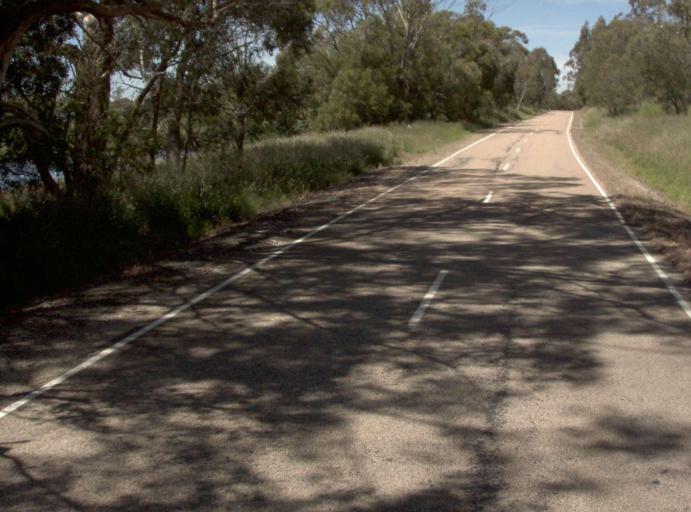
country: AU
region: Victoria
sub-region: East Gippsland
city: Lakes Entrance
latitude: -37.1813
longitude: 148.2693
